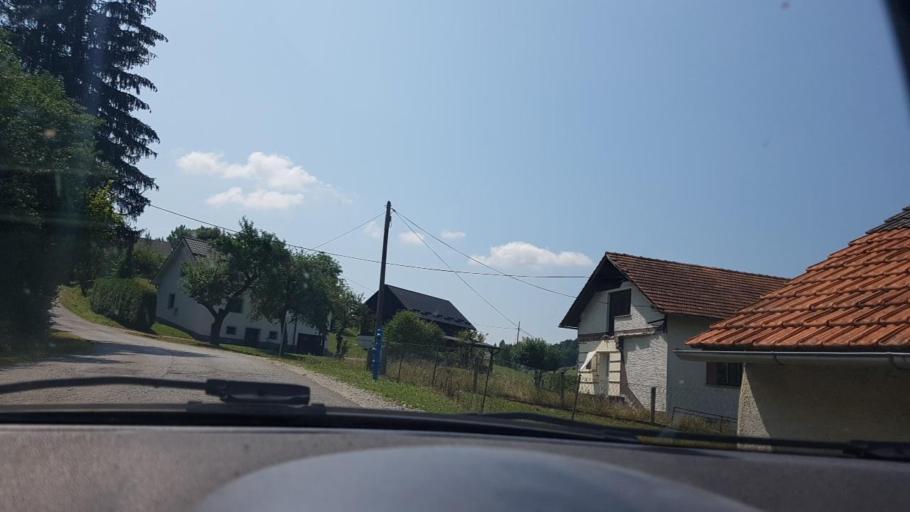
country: SI
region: Rogaska Slatina
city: Rogaska Slatina
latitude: 46.2125
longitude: 15.6462
